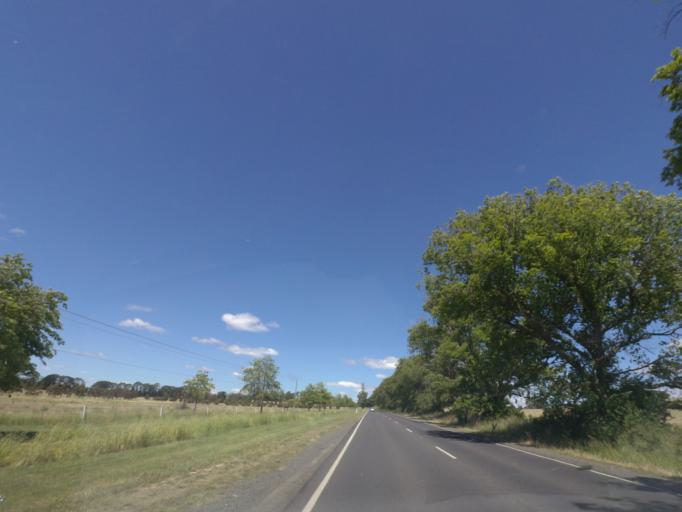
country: AU
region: Victoria
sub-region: Mount Alexander
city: Castlemaine
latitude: -37.2392
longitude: 144.4272
